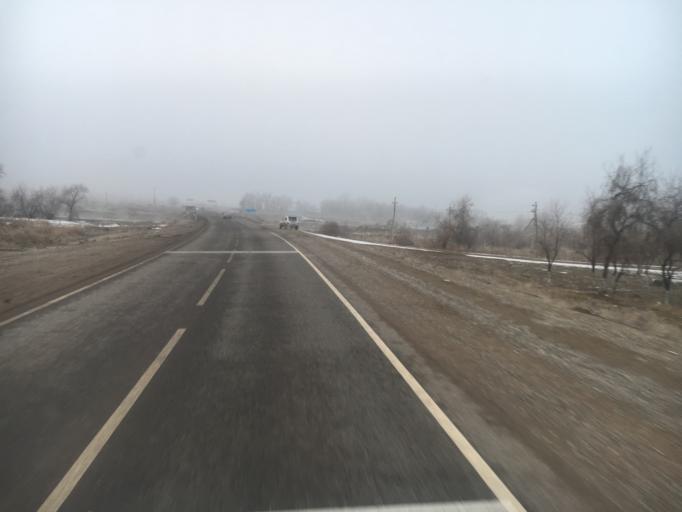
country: KZ
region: Zhambyl
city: Sarykemer
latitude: 43.0399
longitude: 71.5390
